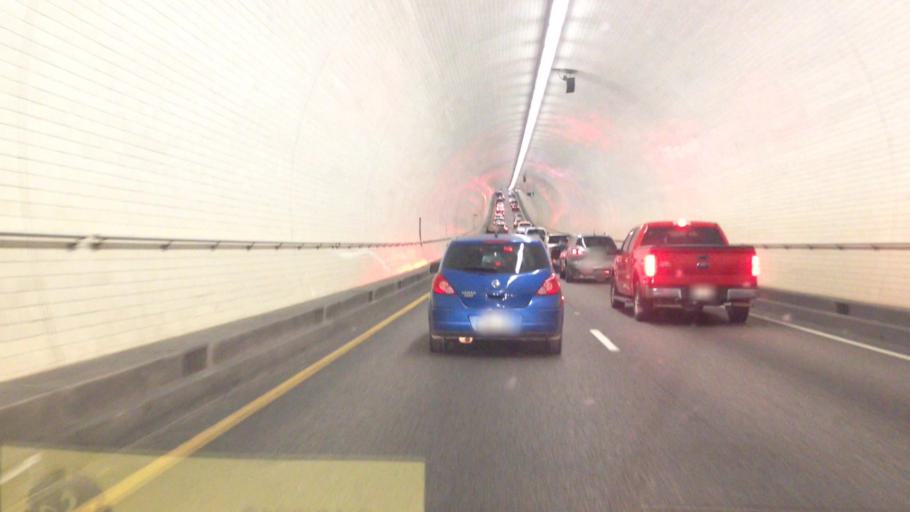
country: US
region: Alabama
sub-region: Mobile County
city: Mobile
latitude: 30.6900
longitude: -88.0358
